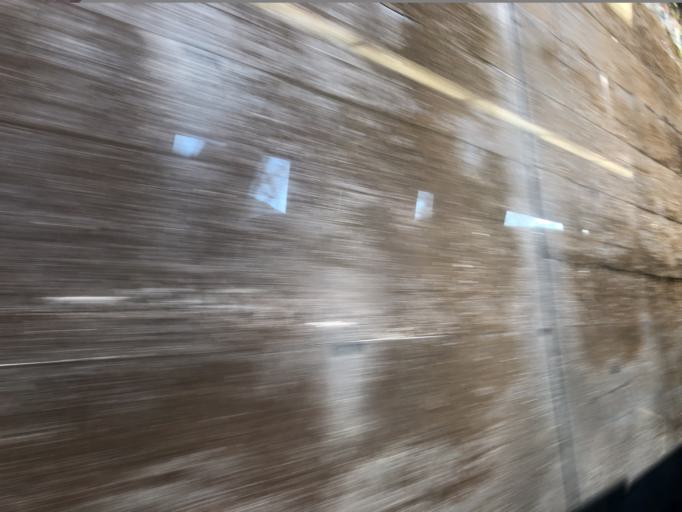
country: JP
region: Kochi
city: Nakamura
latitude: 33.0123
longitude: 132.9907
